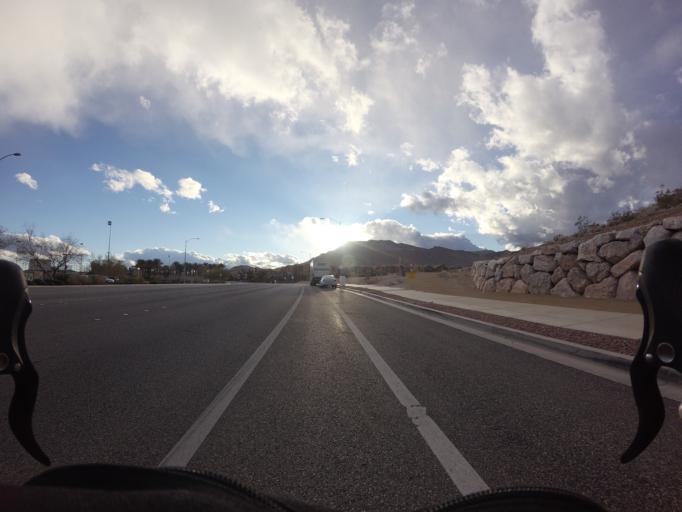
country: US
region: Nevada
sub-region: Clark County
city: Summerlin South
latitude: 36.2328
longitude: -115.3125
